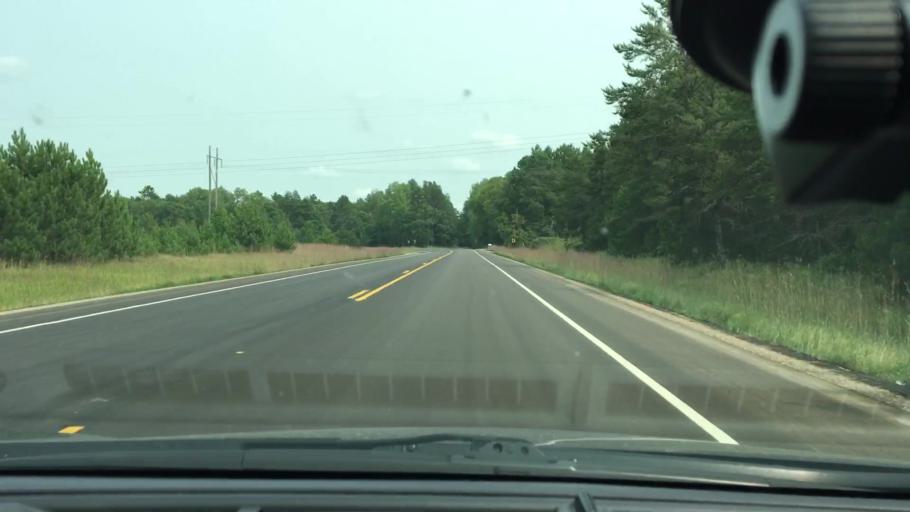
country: US
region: Minnesota
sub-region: Crow Wing County
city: Nisswa
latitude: 46.5300
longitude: -94.2318
